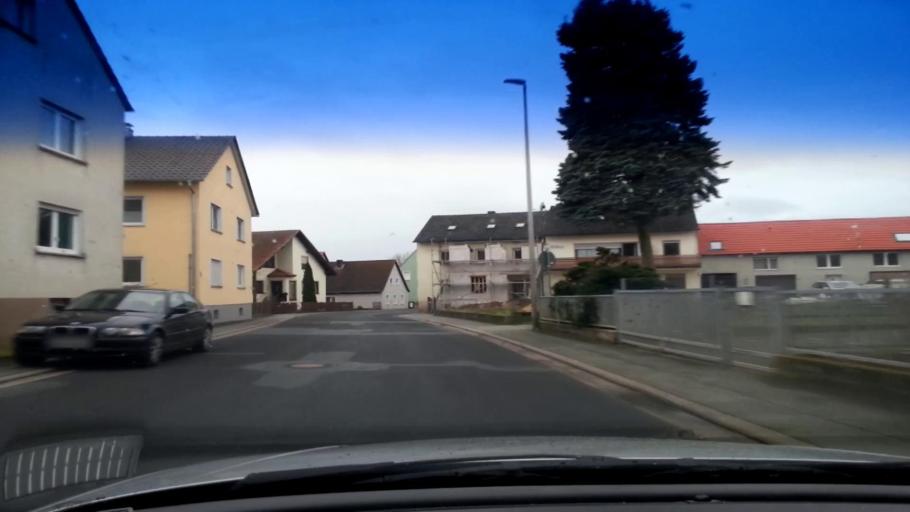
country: DE
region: Bavaria
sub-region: Upper Franconia
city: Frensdorf
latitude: 49.8231
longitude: 10.8913
